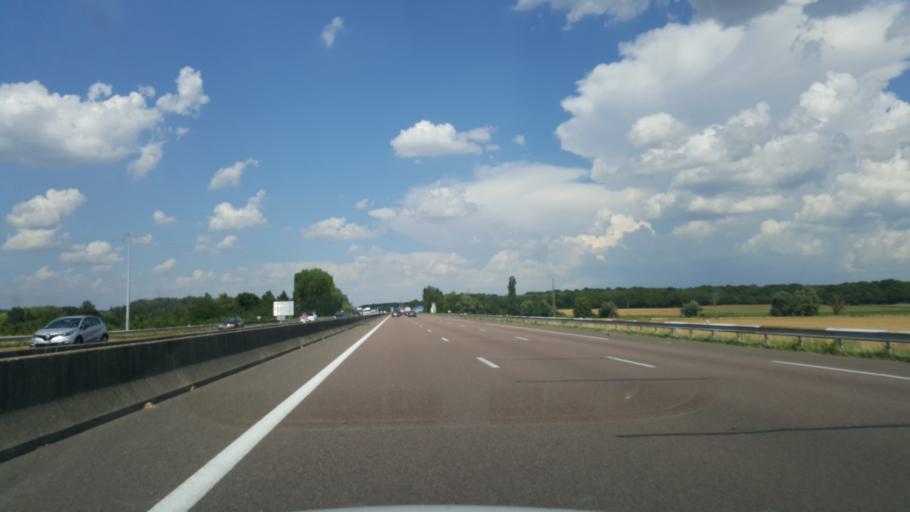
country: FR
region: Bourgogne
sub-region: Departement de Saone-et-Loire
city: Demigny
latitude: 46.9501
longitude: 4.8309
